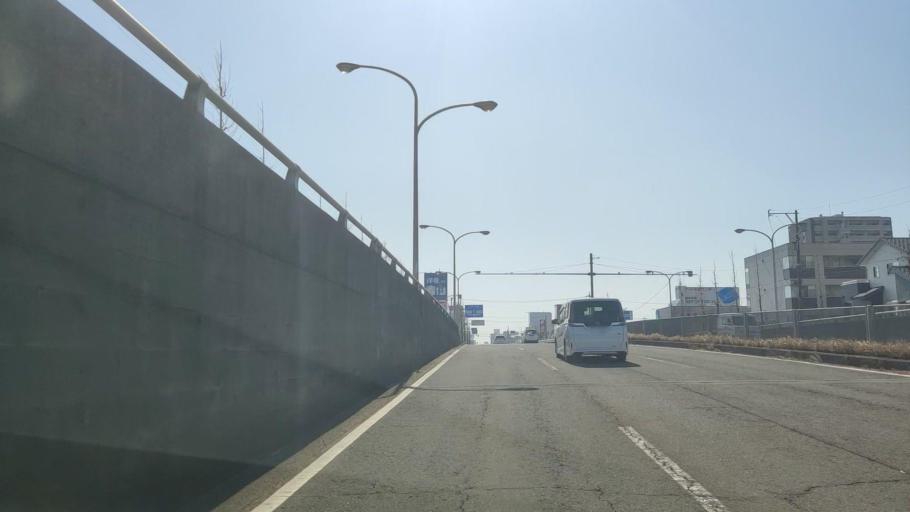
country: JP
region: Gifu
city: Gifu-shi
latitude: 35.4047
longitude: 136.7267
